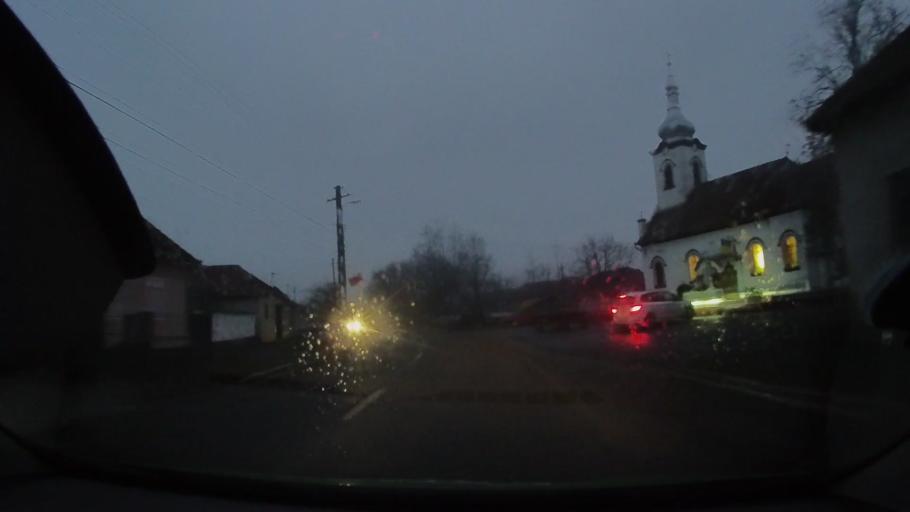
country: RO
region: Arad
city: Hatzmas
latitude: 46.5034
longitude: 22.0766
